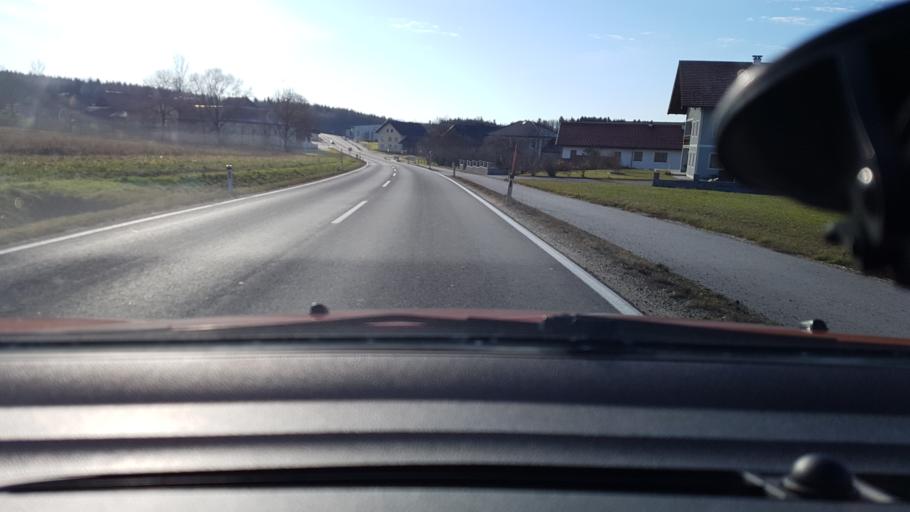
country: AT
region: Salzburg
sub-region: Politischer Bezirk Salzburg-Umgebung
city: Dorfbeuern
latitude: 48.0326
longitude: 12.9762
